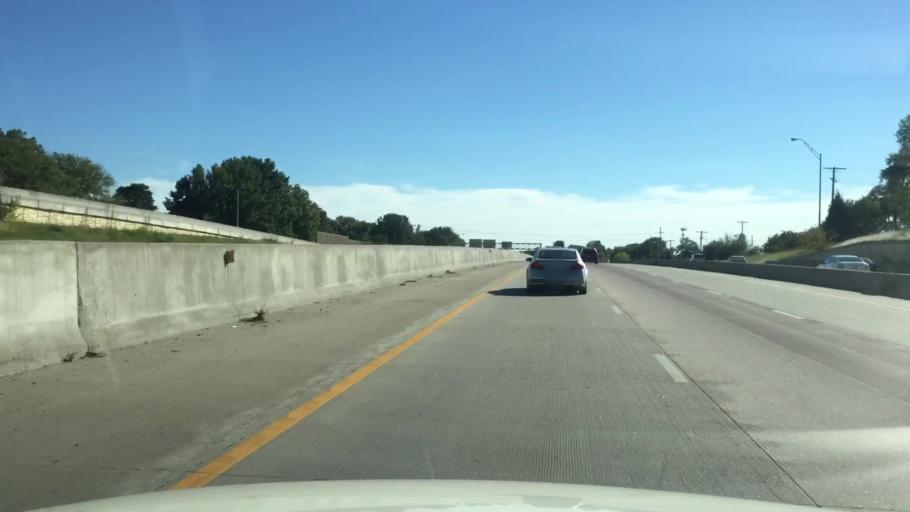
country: US
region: Kansas
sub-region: Johnson County
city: Lenexa
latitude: 38.9694
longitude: -94.7138
